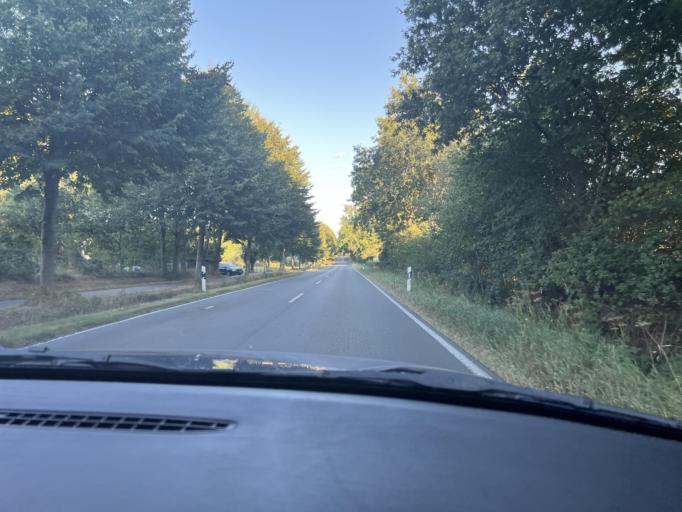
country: DE
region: Schleswig-Holstein
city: Fedderingen
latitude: 54.2906
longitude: 9.1421
